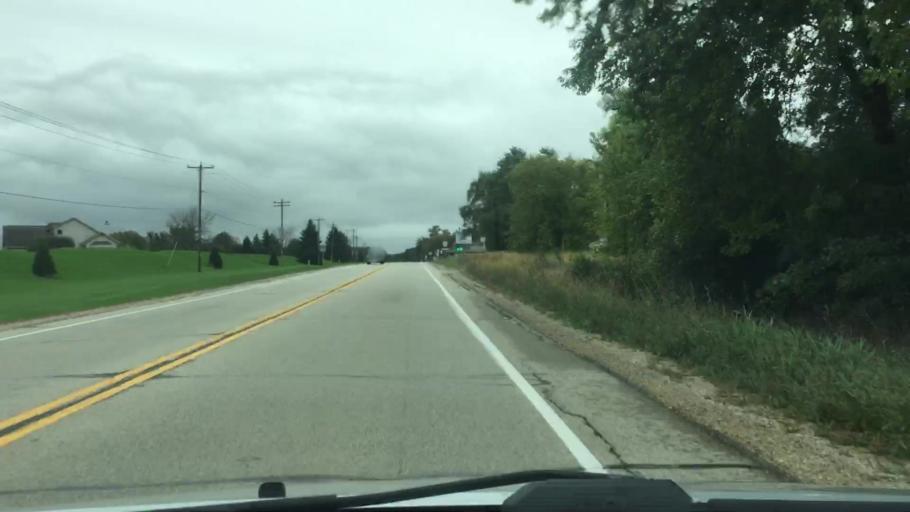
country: US
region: Wisconsin
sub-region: Walworth County
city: Elkhorn
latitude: 42.7510
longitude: -88.5536
